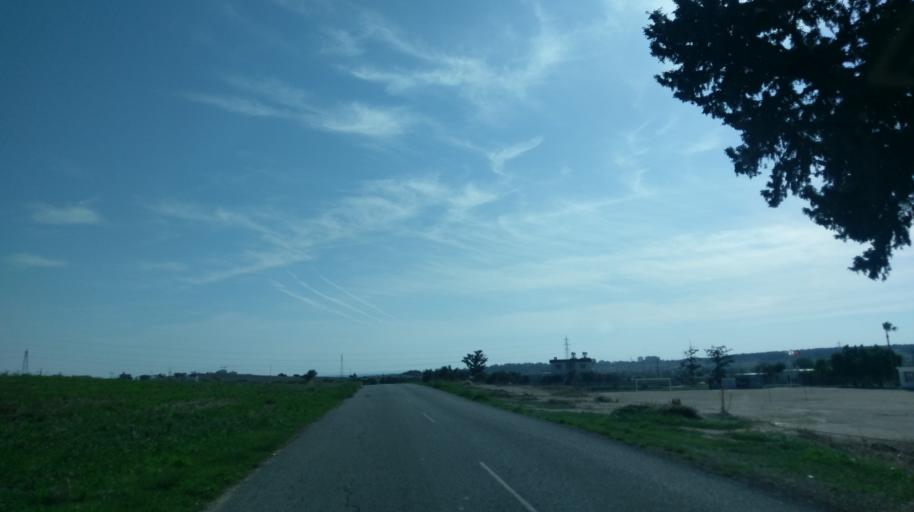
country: CY
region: Ammochostos
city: Trikomo
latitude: 35.3264
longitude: 33.9325
